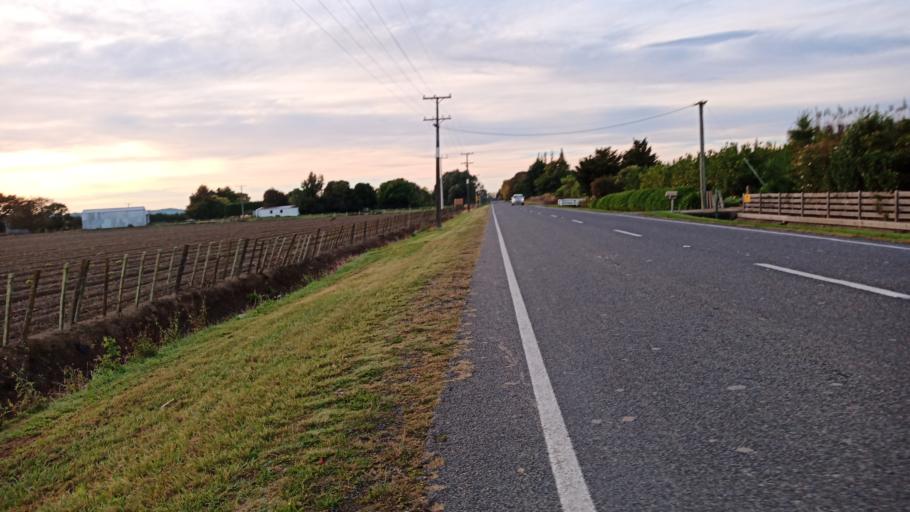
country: NZ
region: Gisborne
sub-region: Gisborne District
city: Gisborne
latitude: -38.6432
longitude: 177.9393
